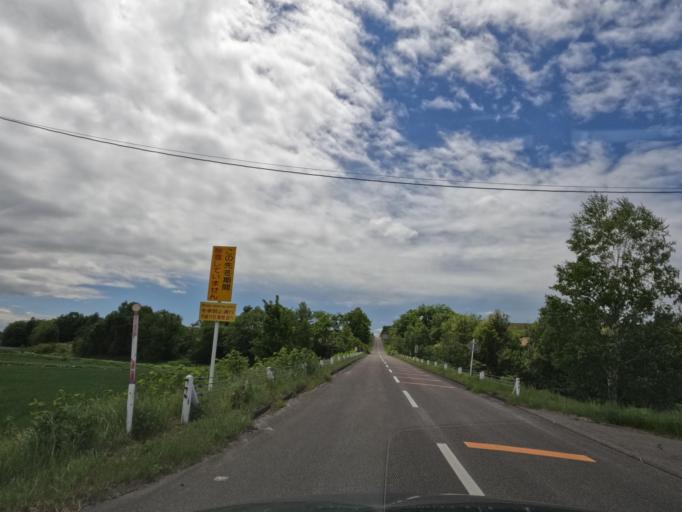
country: JP
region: Hokkaido
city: Shimo-furano
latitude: 43.5141
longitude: 142.4248
